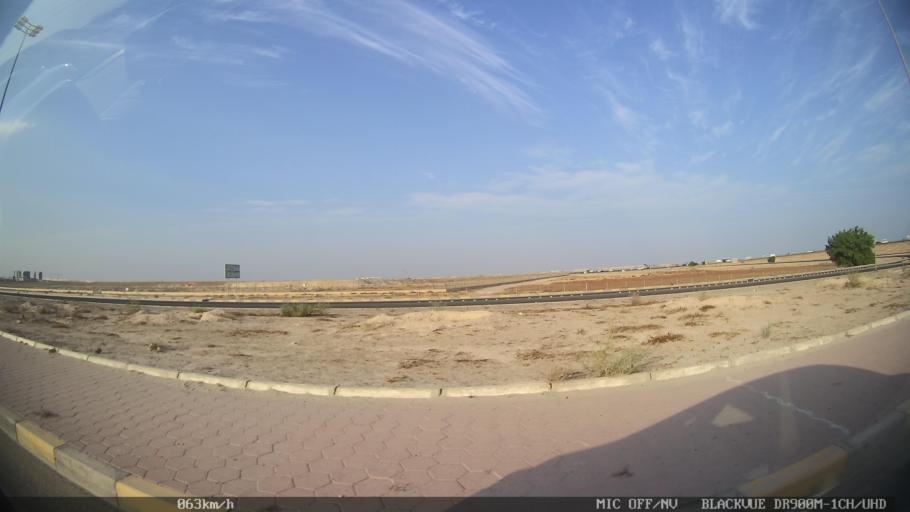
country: KW
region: Al Farwaniyah
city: Janub as Surrah
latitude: 29.1977
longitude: 48.0040
